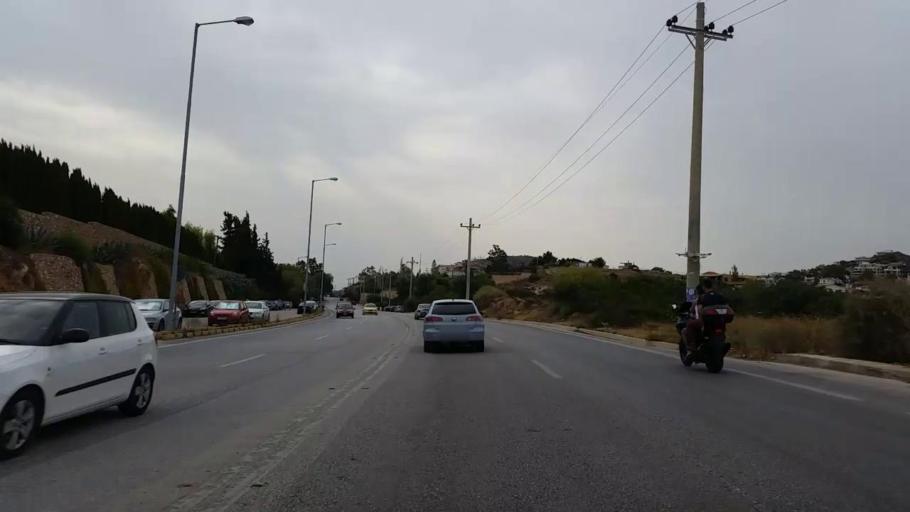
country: GR
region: Attica
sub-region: Nomarchia Anatolikis Attikis
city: Agios Dimitrios Kropias
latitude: 37.7919
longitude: 23.8795
